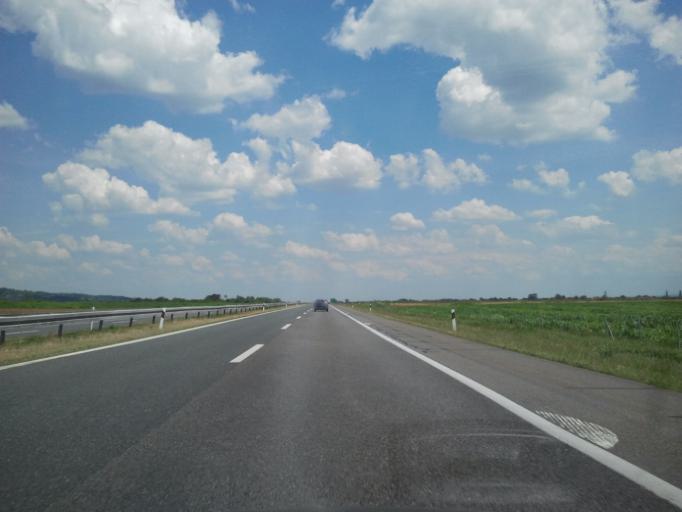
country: HR
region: Brodsko-Posavska
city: Sibinj
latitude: 45.1691
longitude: 17.9023
